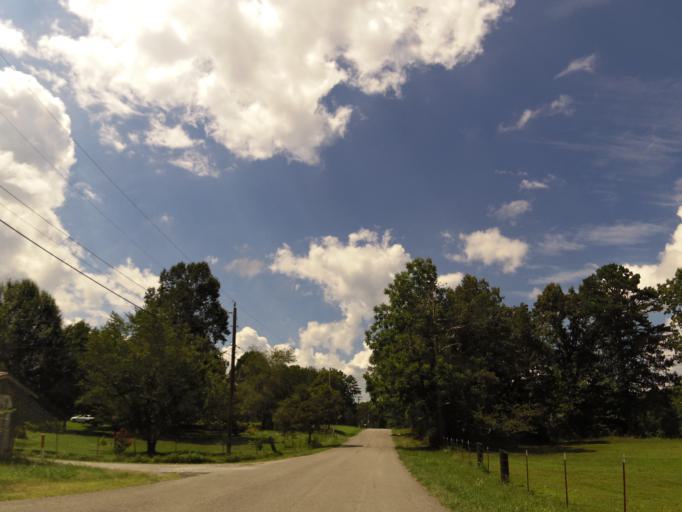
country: US
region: Tennessee
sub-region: Roane County
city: Rockwood
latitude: 35.8957
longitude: -84.7640
